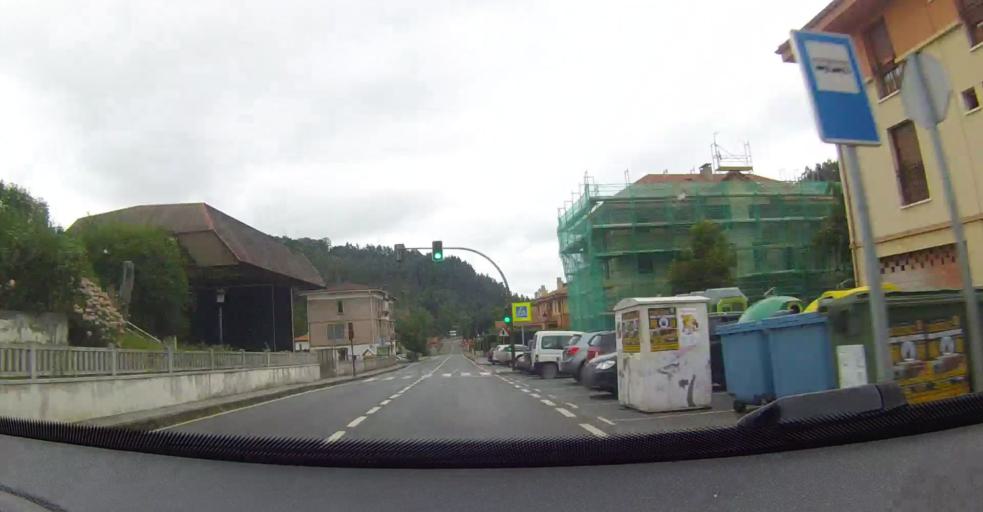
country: ES
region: Basque Country
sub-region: Bizkaia
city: Balmaseda
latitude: 43.2411
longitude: -3.2146
